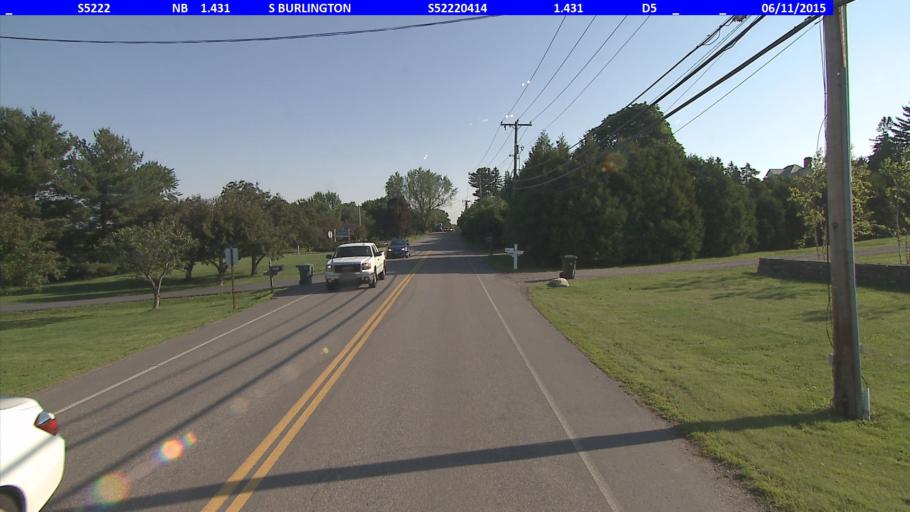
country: US
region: Vermont
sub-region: Chittenden County
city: South Burlington
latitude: 44.4373
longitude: -73.1910
